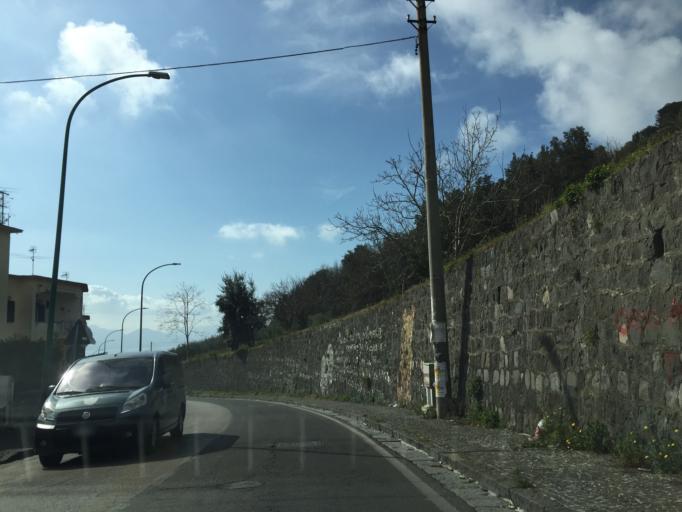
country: IT
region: Campania
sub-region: Provincia di Napoli
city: Torre del Greco
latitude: 40.7822
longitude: 14.4081
